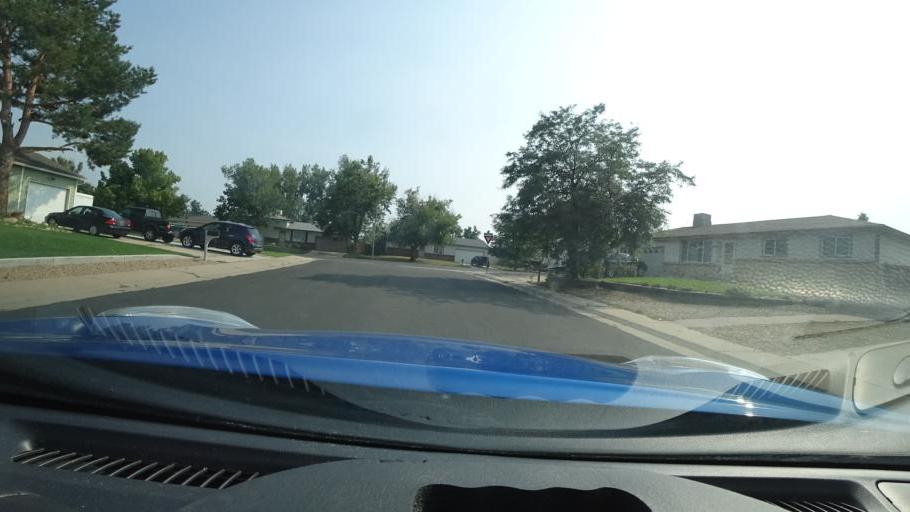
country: US
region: Colorado
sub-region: Adams County
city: Aurora
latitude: 39.6649
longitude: -104.8090
